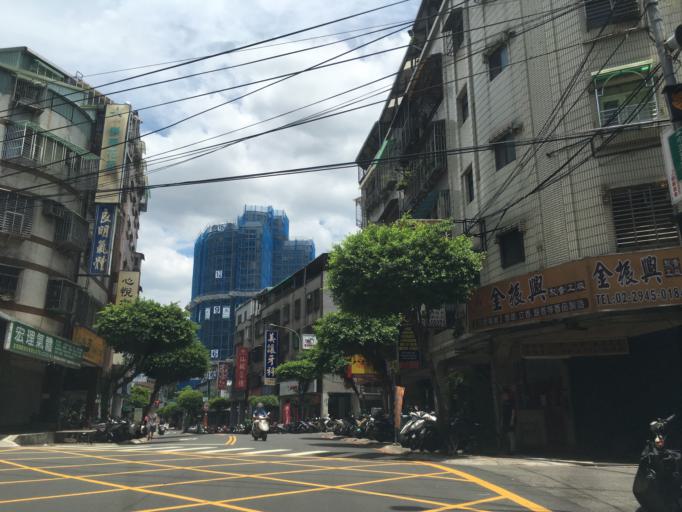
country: TW
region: Taipei
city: Taipei
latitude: 25.0001
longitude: 121.5163
